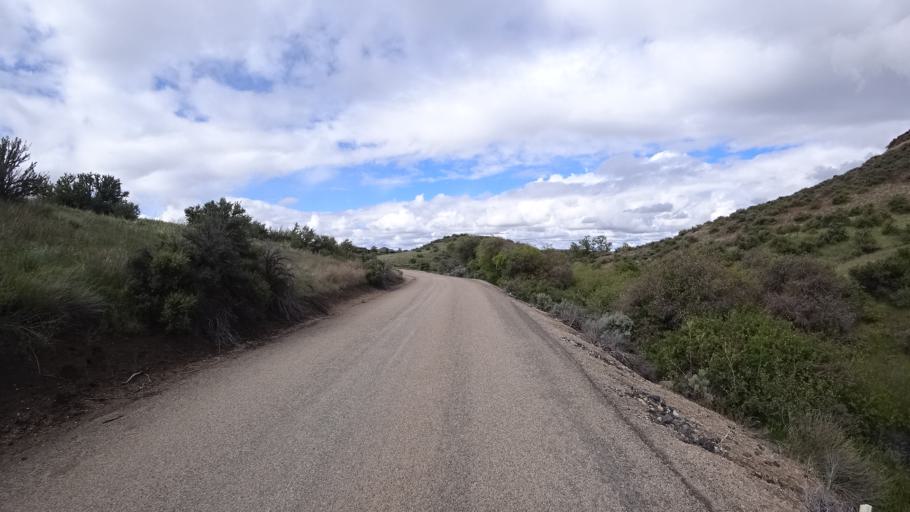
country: US
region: Idaho
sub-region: Ada County
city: Garden City
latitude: 43.7285
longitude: -116.2322
